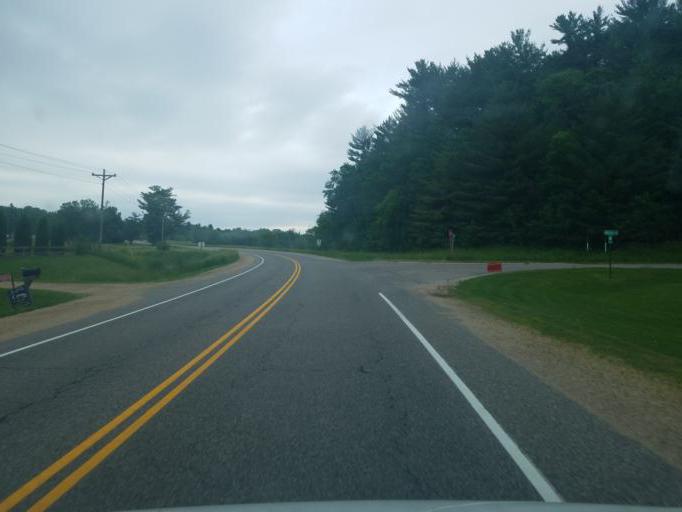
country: US
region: Wisconsin
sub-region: Juneau County
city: Elroy
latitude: 43.7607
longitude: -90.2659
